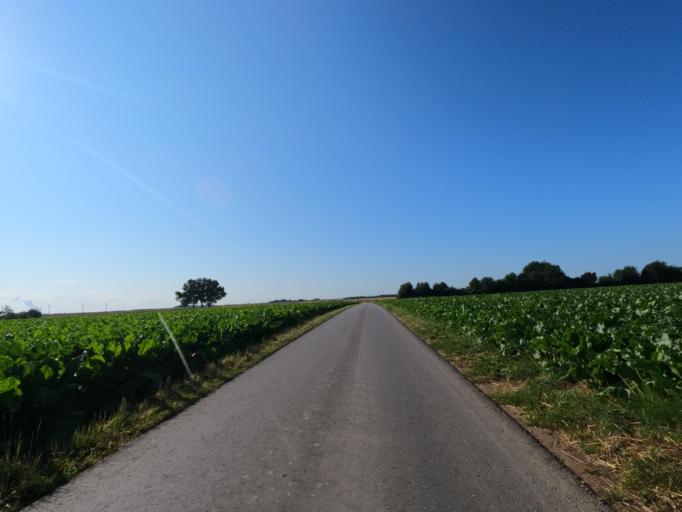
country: DE
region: North Rhine-Westphalia
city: Erkelenz
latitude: 51.0754
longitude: 6.3673
